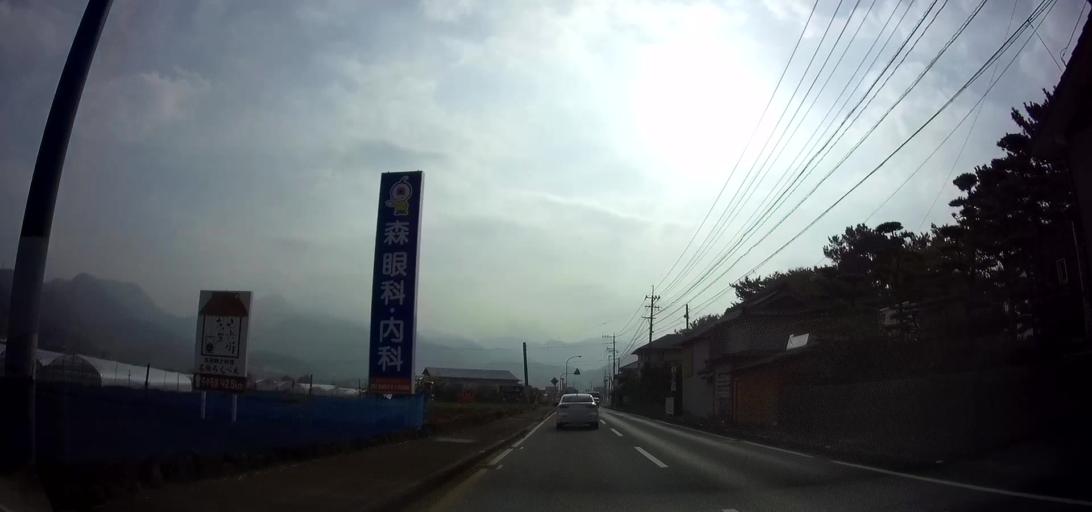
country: JP
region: Nagasaki
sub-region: Isahaya-shi
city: Isahaya
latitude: 32.7920
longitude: 130.1851
